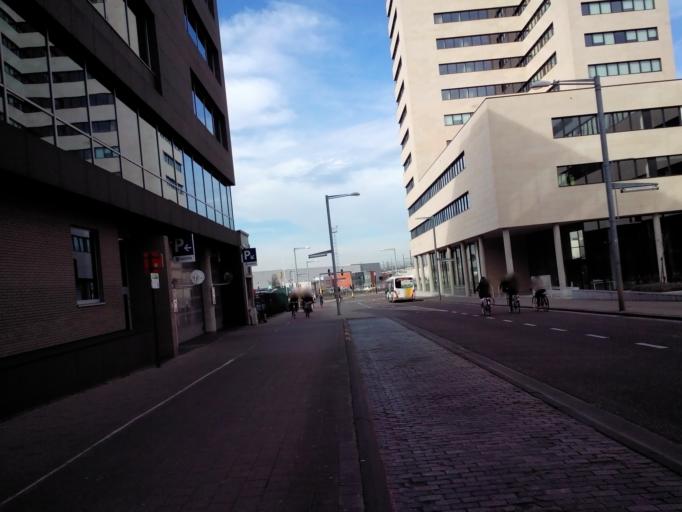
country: BE
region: Flanders
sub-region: Provincie Vlaams-Brabant
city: Leuven
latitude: 50.8830
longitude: 4.7143
